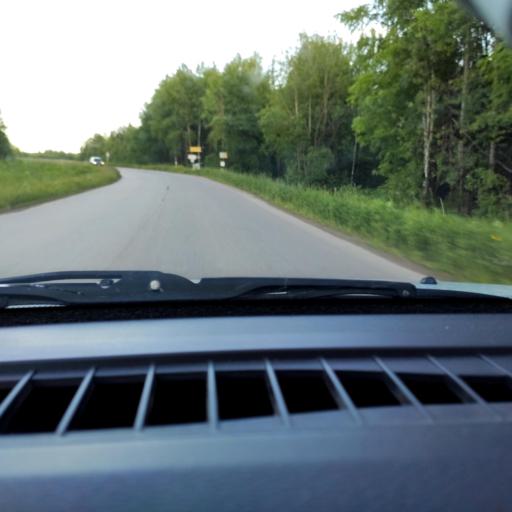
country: RU
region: Perm
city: Polazna
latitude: 58.2106
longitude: 56.4474
